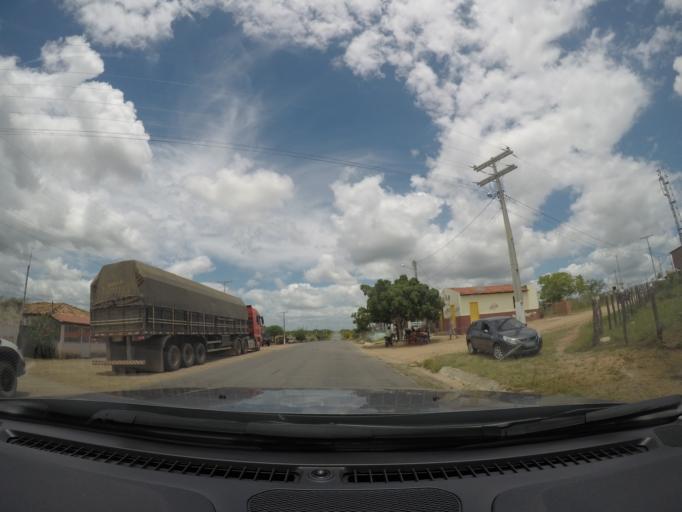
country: BR
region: Bahia
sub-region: Ipira
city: Ipira
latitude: -12.3020
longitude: -39.8950
